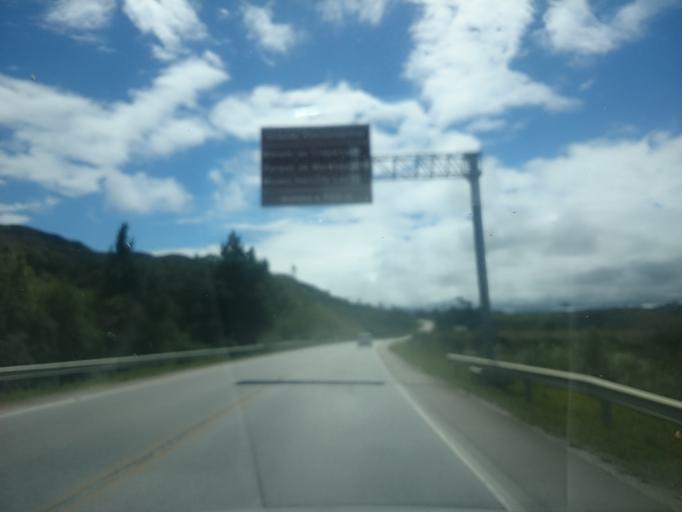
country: BR
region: Santa Catarina
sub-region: Anitapolis
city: Anitapolis
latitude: -27.6775
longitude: -49.1468
